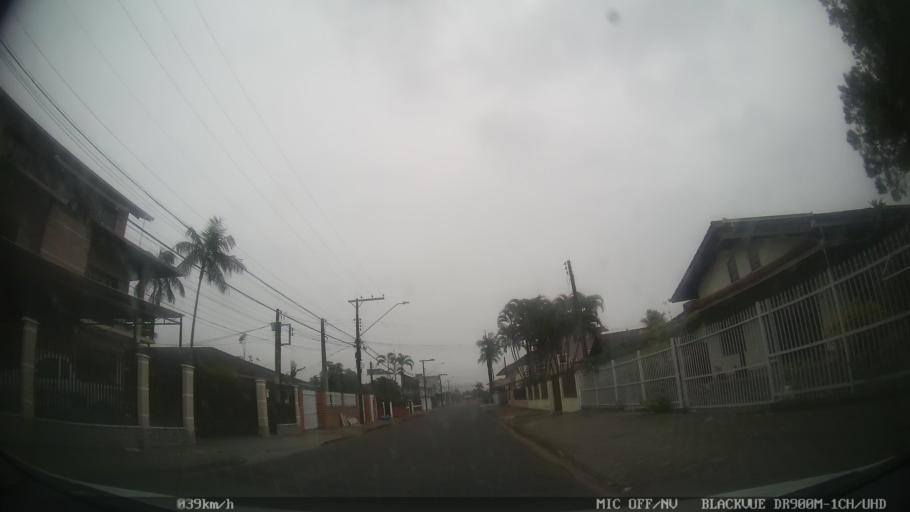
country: BR
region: Santa Catarina
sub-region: Joinville
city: Joinville
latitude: -26.2802
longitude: -48.8012
